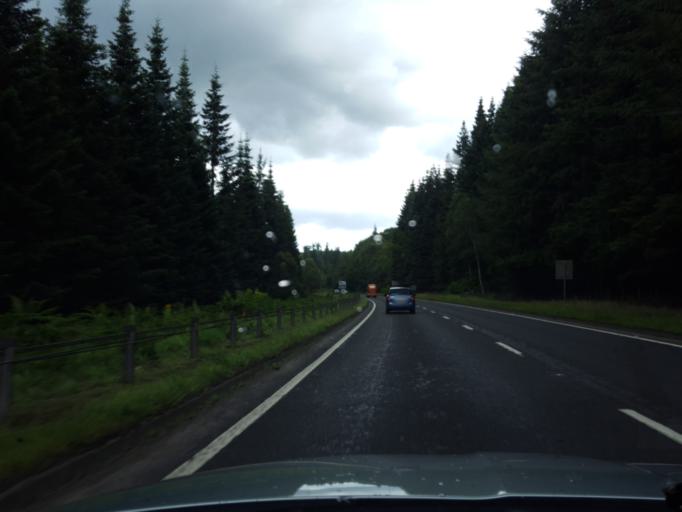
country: GB
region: Scotland
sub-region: Perth and Kinross
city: Bankfoot
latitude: 56.5407
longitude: -3.5482
